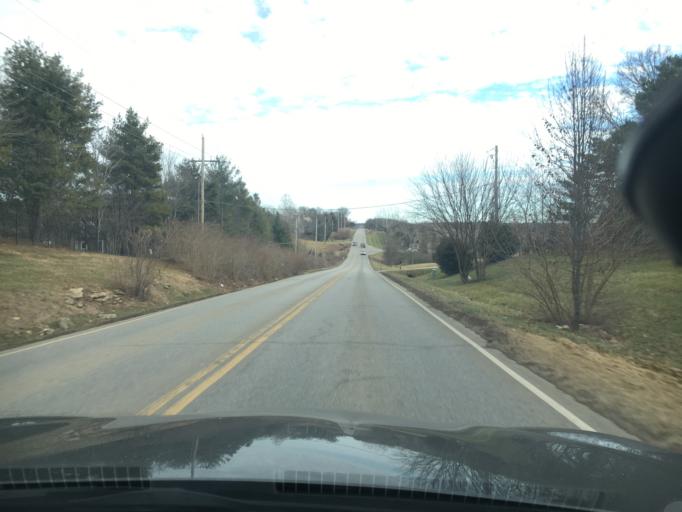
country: US
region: Missouri
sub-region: Jackson County
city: Grandview
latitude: 38.8547
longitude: -94.6369
